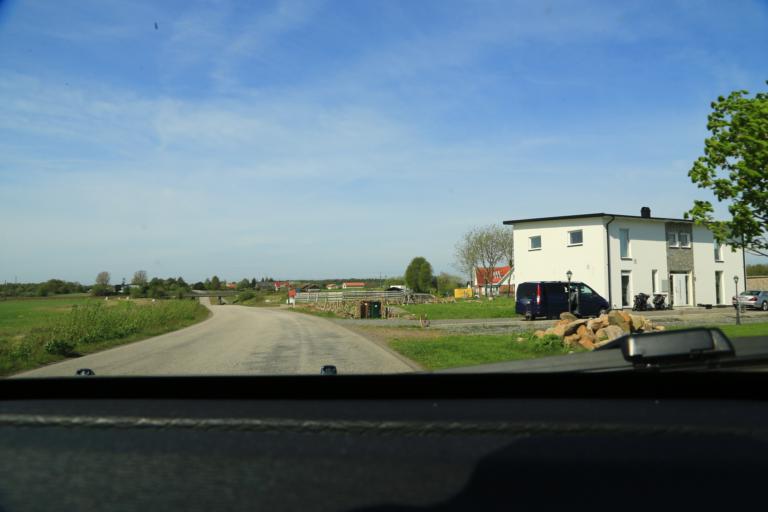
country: SE
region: Halland
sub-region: Varbergs Kommun
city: Varberg
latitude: 57.1506
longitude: 12.2556
